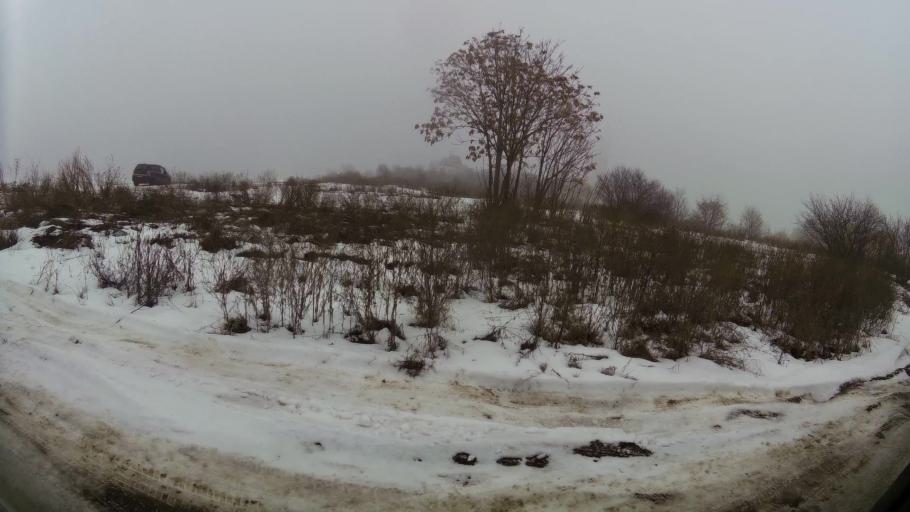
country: RO
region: Ilfov
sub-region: Comuna Chiajna
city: Rosu
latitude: 44.4459
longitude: 26.0339
